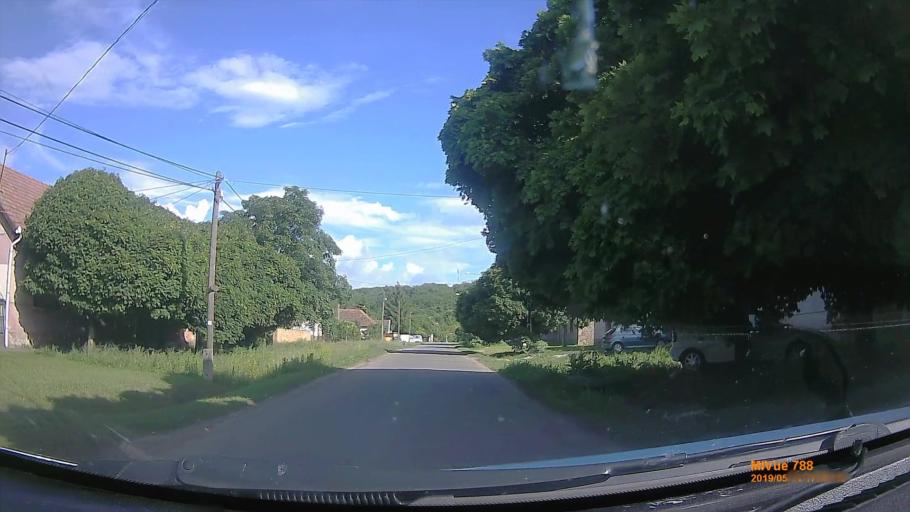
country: HU
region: Nograd
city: Nagyoroszi
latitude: 48.0445
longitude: 19.0542
